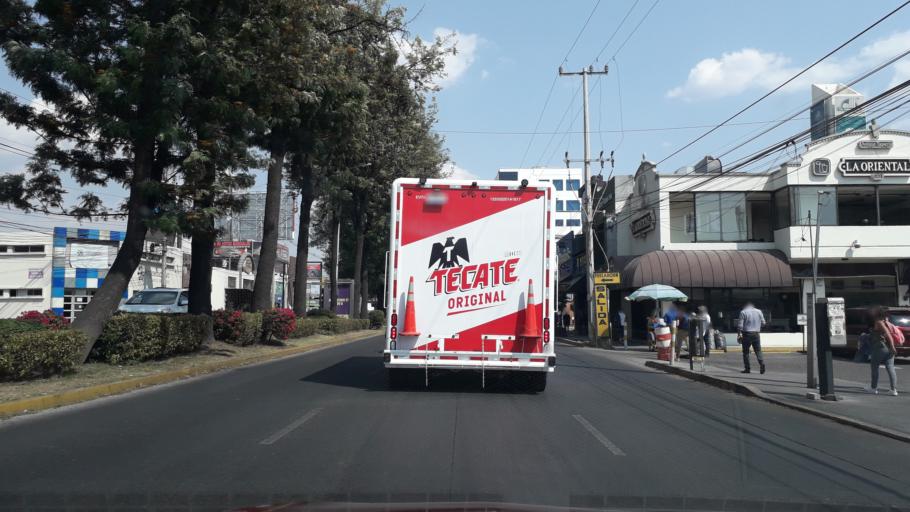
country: MX
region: Puebla
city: Puebla
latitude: 19.0408
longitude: -98.2289
